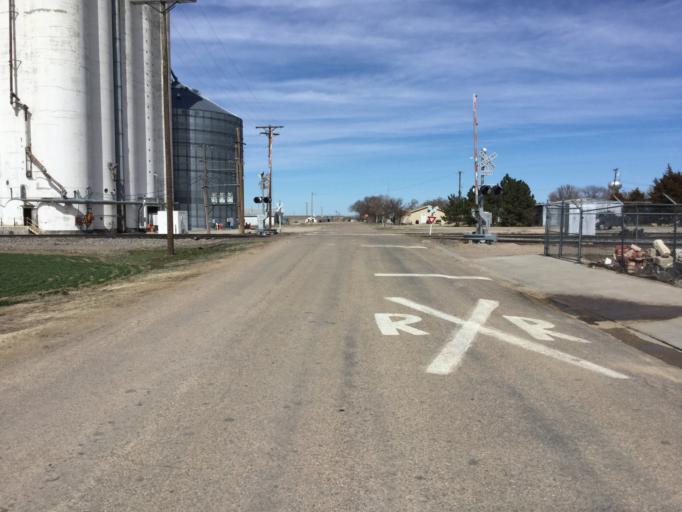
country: US
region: Kansas
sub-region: Greeley County
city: Tribune
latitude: 38.4682
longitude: -101.7613
